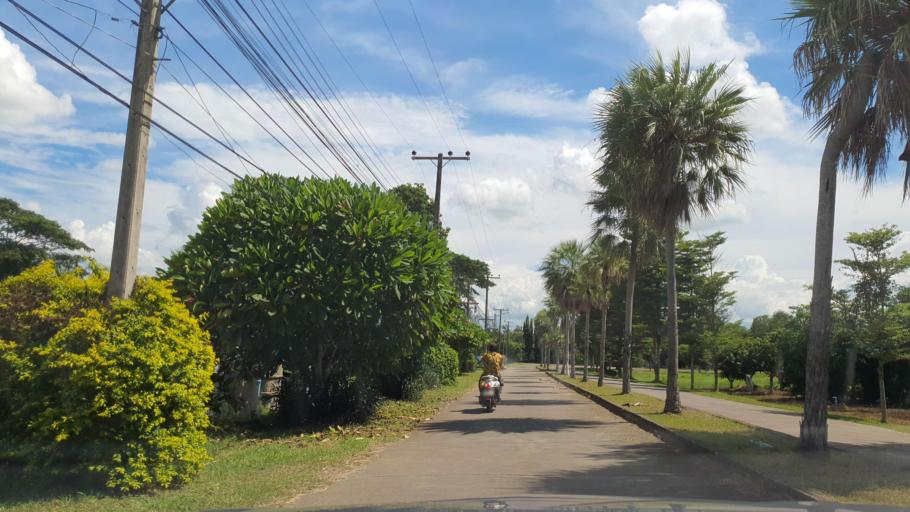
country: TH
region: Chiang Mai
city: San Pa Tong
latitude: 18.5915
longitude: 98.8751
